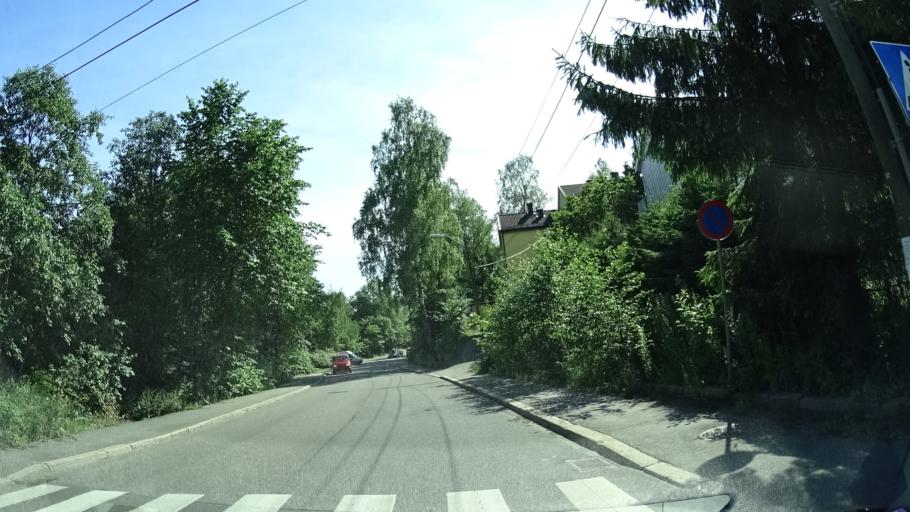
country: NO
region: Oslo
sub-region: Oslo
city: Oslo
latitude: 59.9631
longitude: 10.7696
